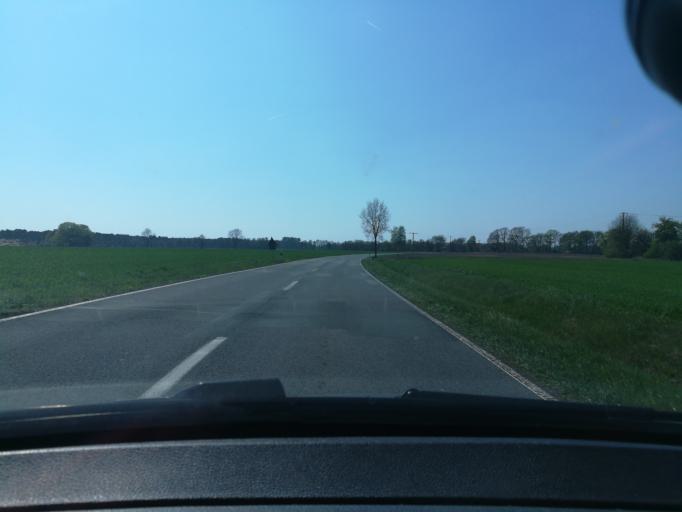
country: DE
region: North Rhine-Westphalia
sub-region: Regierungsbezirk Detmold
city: Harsewinkel
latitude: 52.0084
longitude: 8.2217
